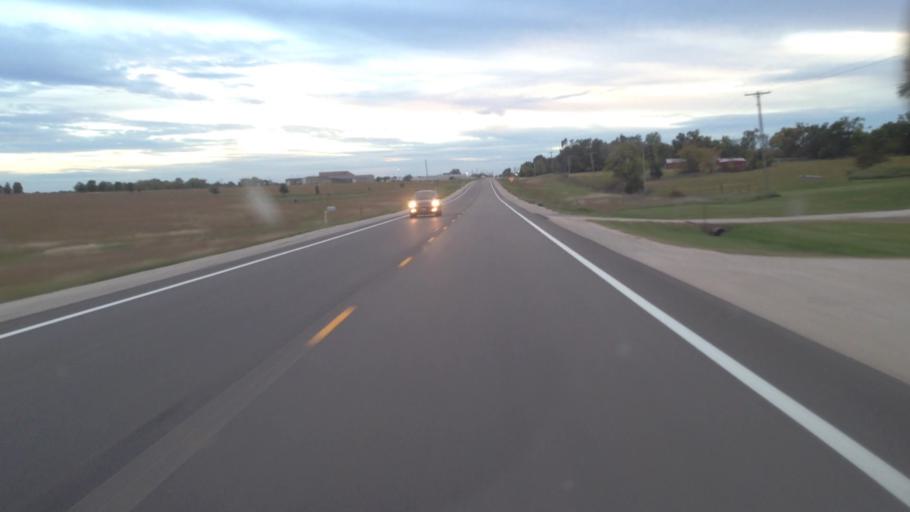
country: US
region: Kansas
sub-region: Anderson County
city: Garnett
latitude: 38.3029
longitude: -95.2489
